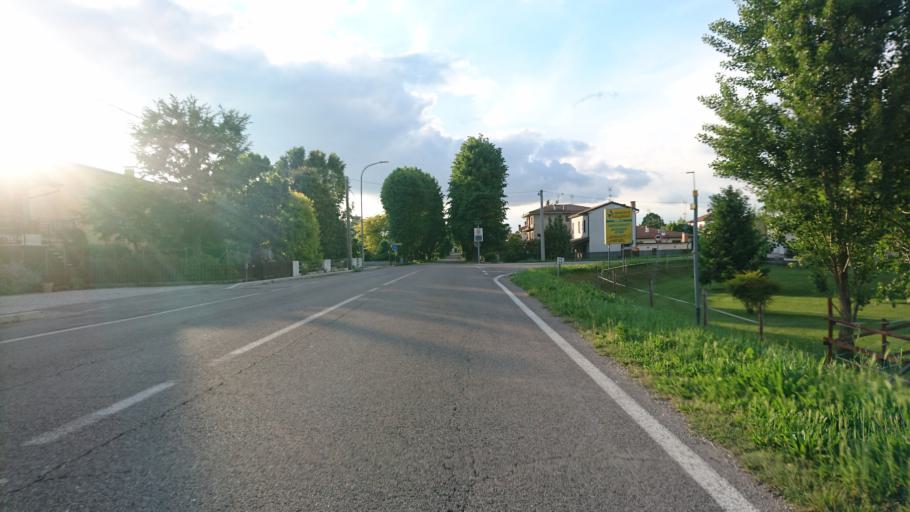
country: IT
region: Veneto
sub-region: Provincia di Rovigo
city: Ceneselli
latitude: 45.0105
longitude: 11.3725
